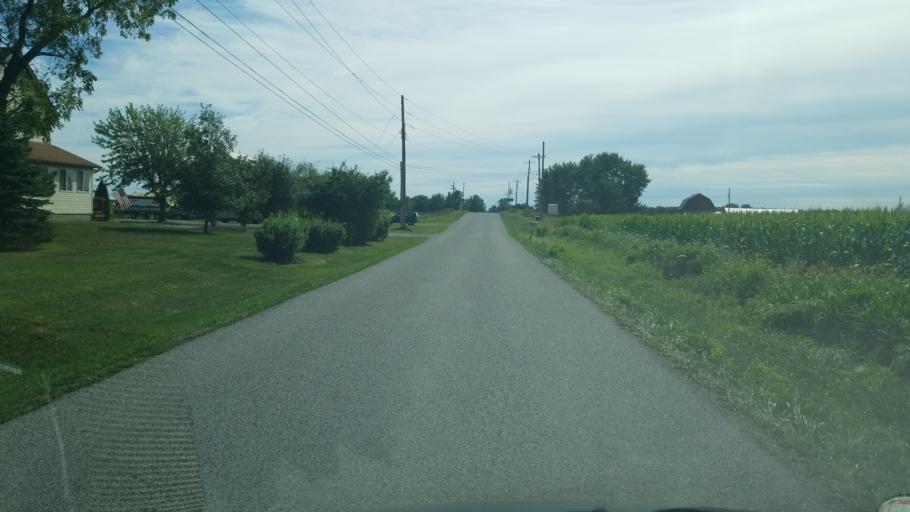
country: US
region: Ohio
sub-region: Delaware County
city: Ashley
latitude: 40.4238
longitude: -82.9480
